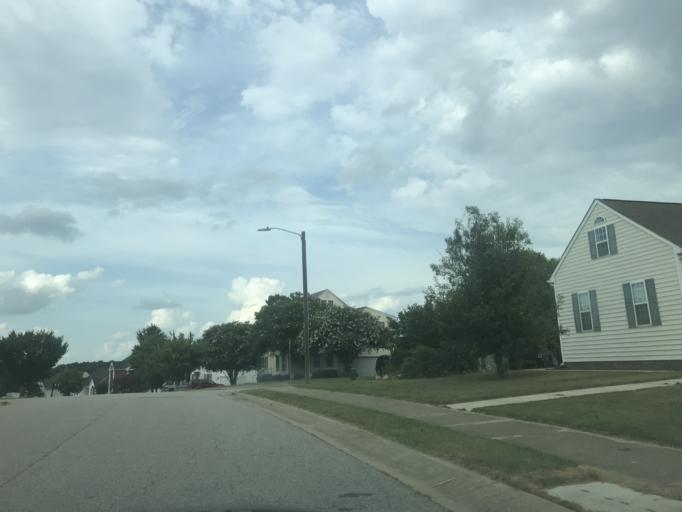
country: US
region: North Carolina
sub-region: Wake County
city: Knightdale
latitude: 35.8351
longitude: -78.5582
